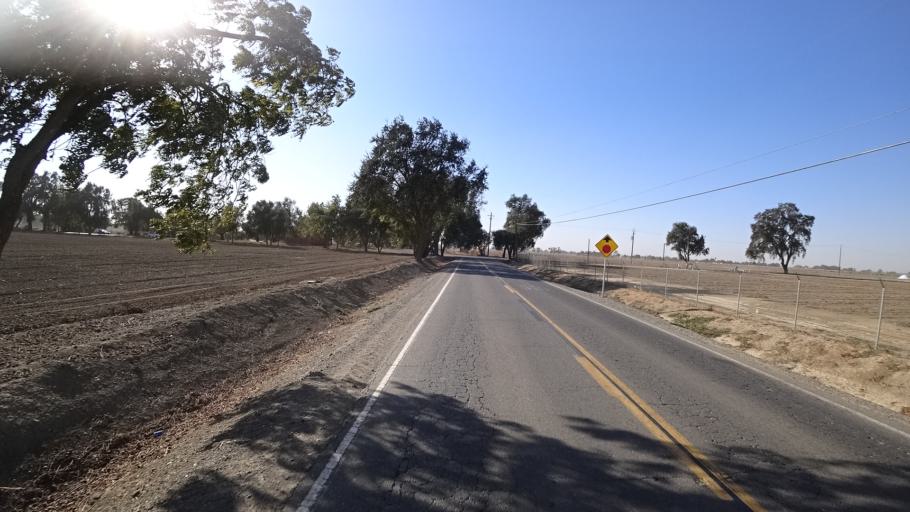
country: US
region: California
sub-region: Yolo County
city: Woodland
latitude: 38.7351
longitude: -121.7640
